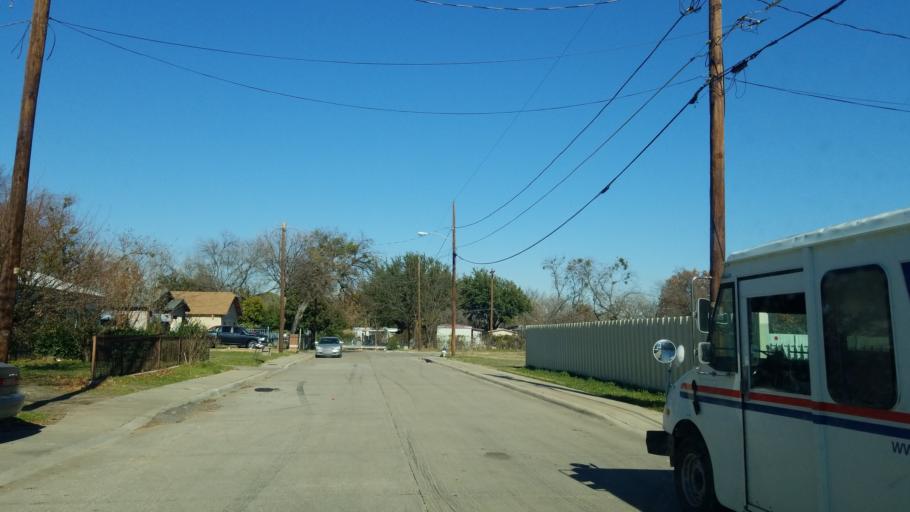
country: US
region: Texas
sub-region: Dallas County
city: Cockrell Hill
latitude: 32.7575
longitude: -96.9141
